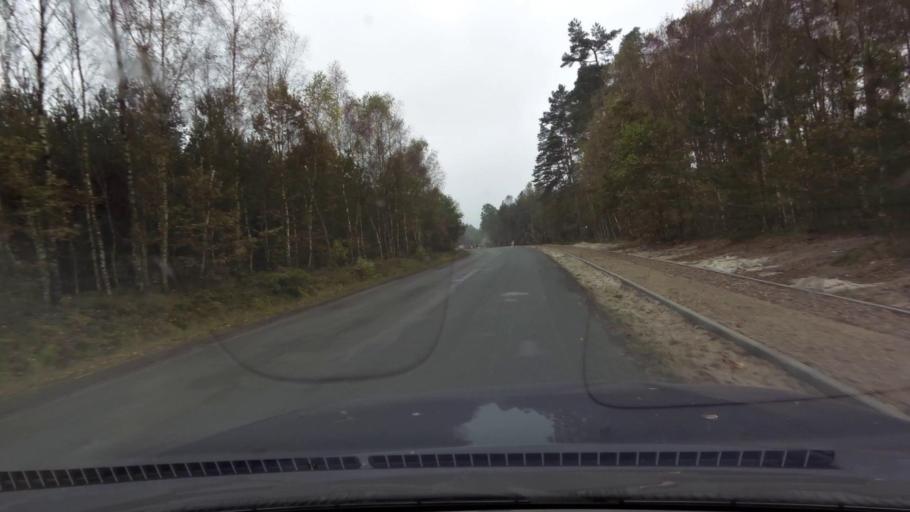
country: PL
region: West Pomeranian Voivodeship
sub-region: Powiat goleniowski
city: Goleniow
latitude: 53.5389
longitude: 14.7660
